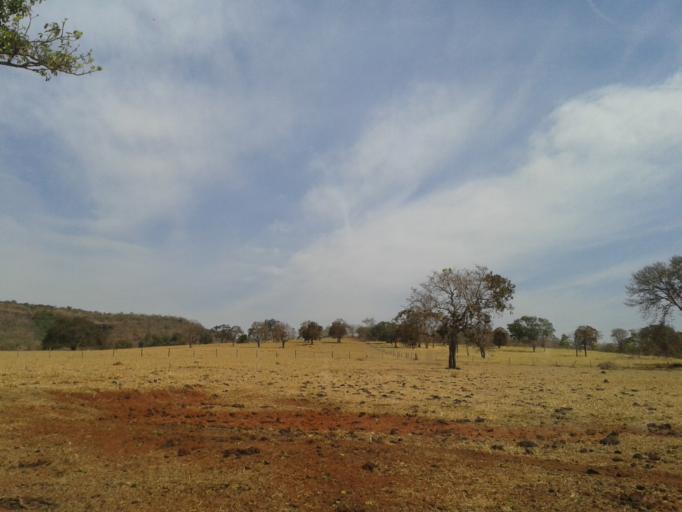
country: BR
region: Minas Gerais
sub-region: Santa Vitoria
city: Santa Vitoria
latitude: -19.2265
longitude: -50.0228
